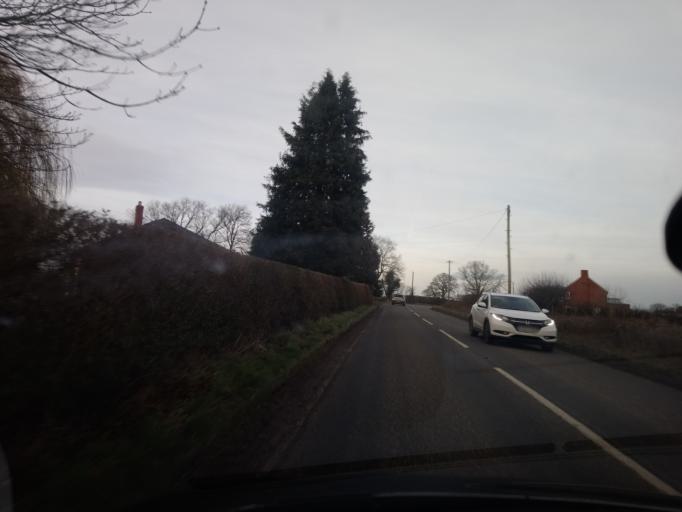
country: GB
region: England
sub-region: Shropshire
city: Prees
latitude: 52.9007
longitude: -2.7063
